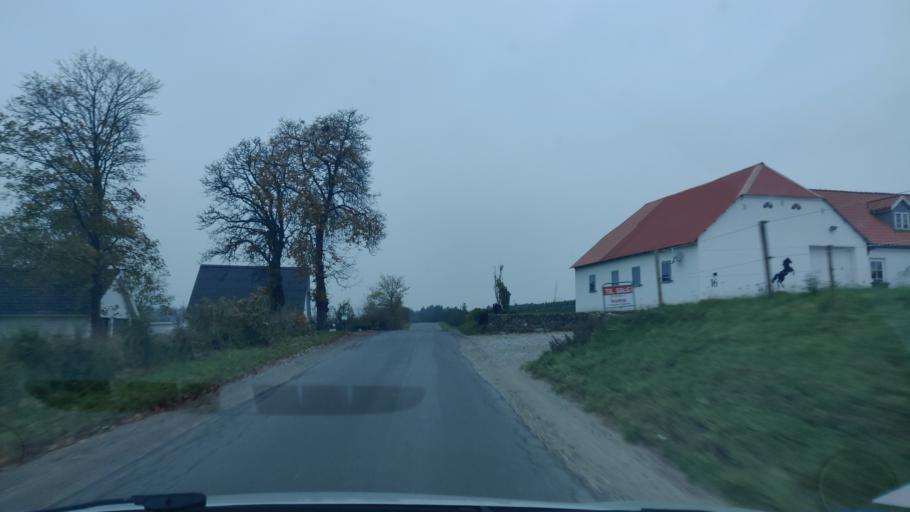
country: DK
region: South Denmark
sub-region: Kolding Kommune
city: Kolding
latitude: 55.5669
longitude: 9.4321
